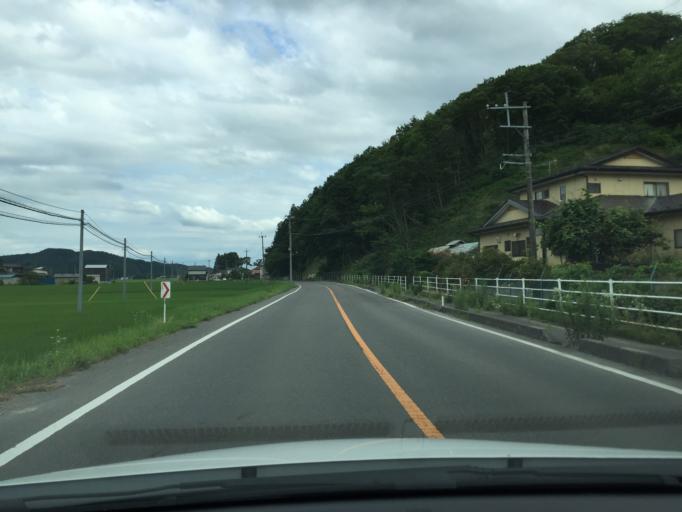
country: JP
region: Tochigi
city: Kuroiso
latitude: 37.1715
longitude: 140.1647
